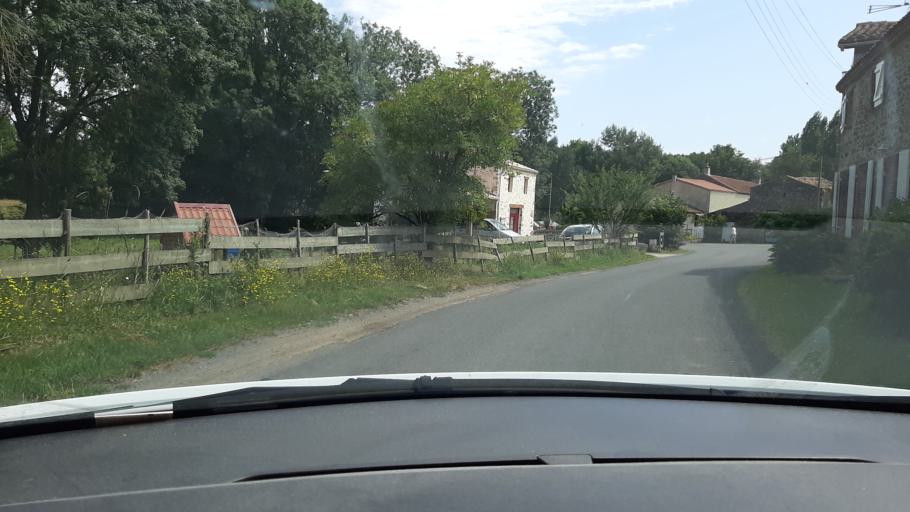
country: FR
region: Pays de la Loire
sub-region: Departement de la Vendee
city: Saint-Etienne-du-Bois
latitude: 46.7831
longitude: -1.5684
